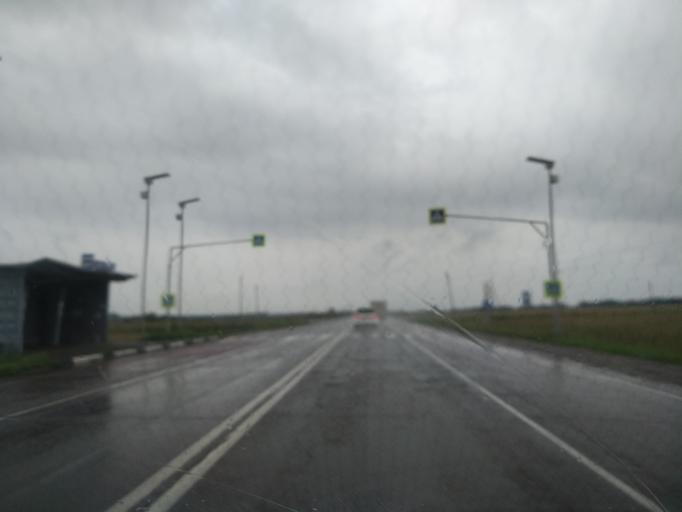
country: RU
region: Voronezj
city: Verkhnyaya Khava
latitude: 51.6780
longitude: 39.8743
